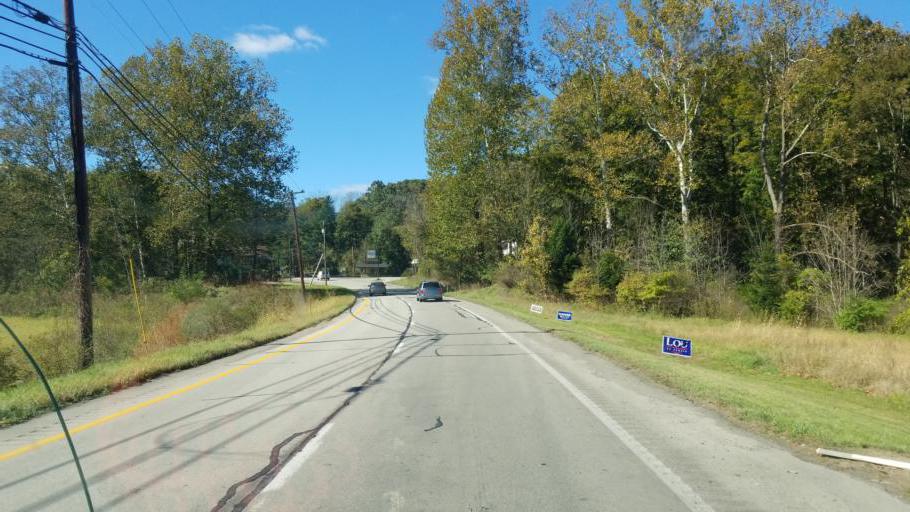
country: US
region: Pennsylvania
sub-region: Westmoreland County
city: Ligonier
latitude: 40.2625
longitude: -79.2681
